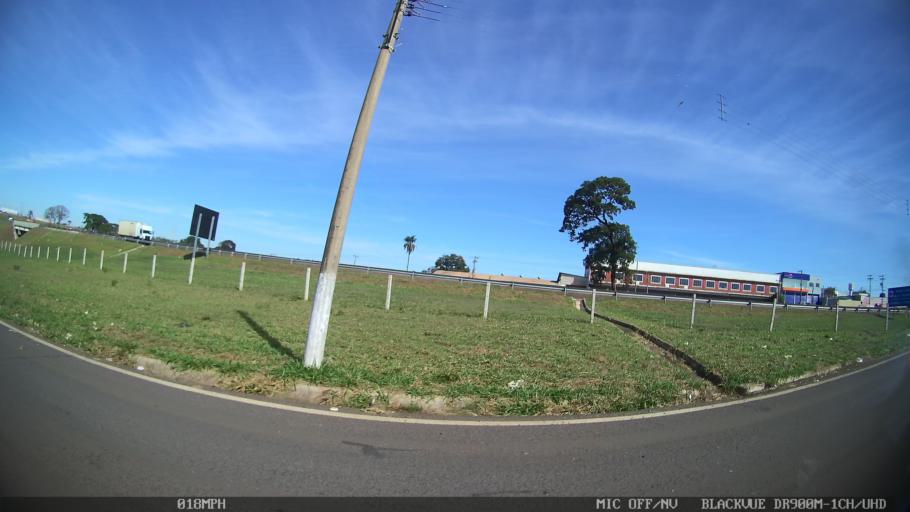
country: BR
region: Sao Paulo
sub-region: Porto Ferreira
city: Porto Ferreira
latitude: -21.8651
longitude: -47.4909
